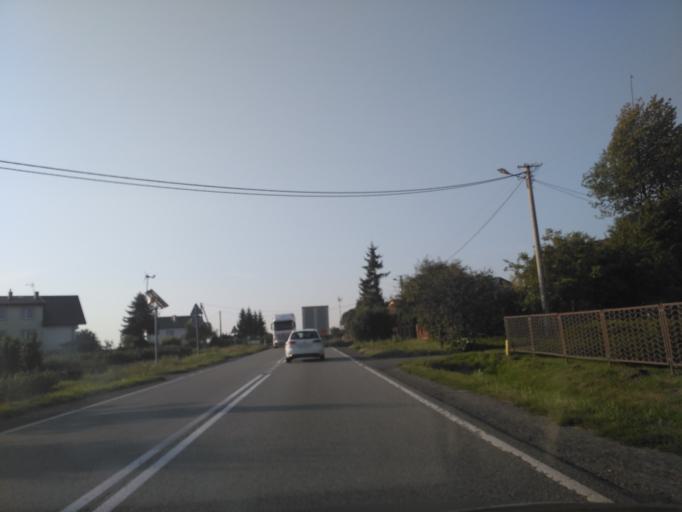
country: PL
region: Lublin Voivodeship
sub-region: Powiat krasnicki
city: Szastarka
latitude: 50.8236
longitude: 22.3144
